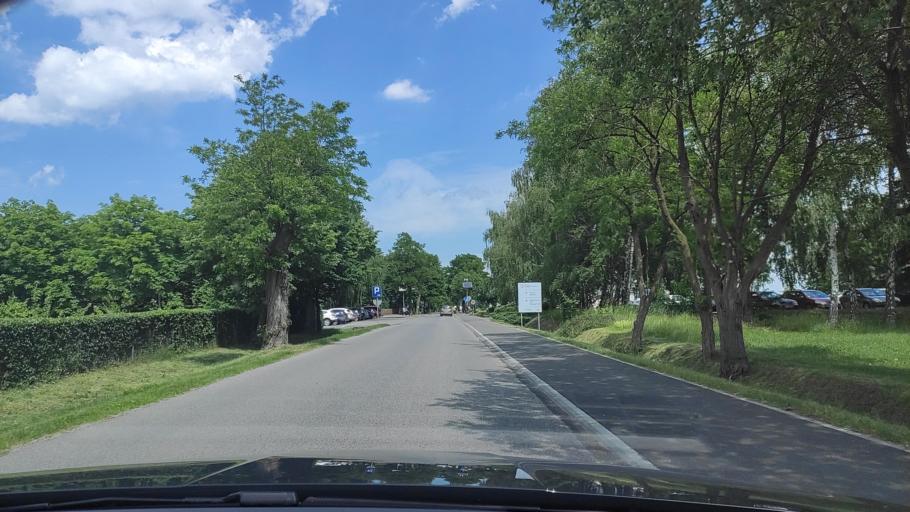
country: PL
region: Greater Poland Voivodeship
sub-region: Powiat gnieznienski
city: Lubowo
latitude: 52.5120
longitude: 17.3836
